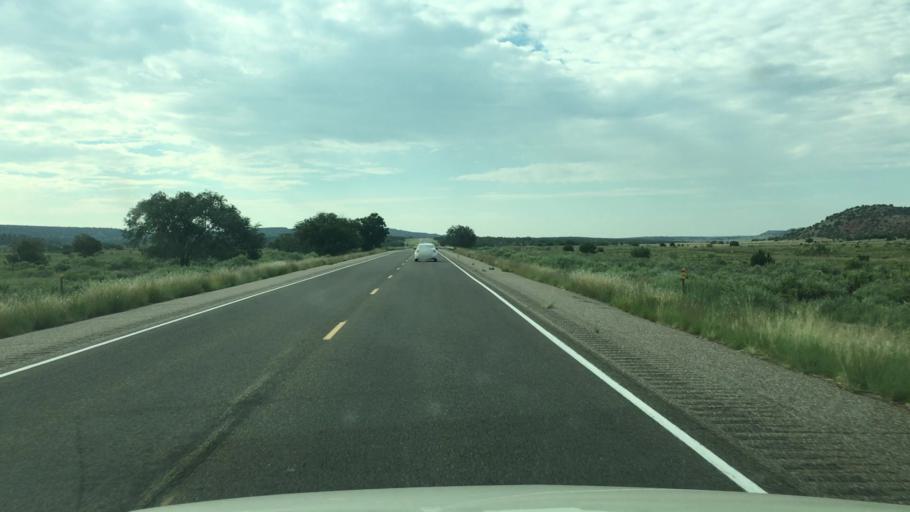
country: US
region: New Mexico
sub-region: Santa Fe County
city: Eldorado at Santa Fe
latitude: 35.3454
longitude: -105.8429
